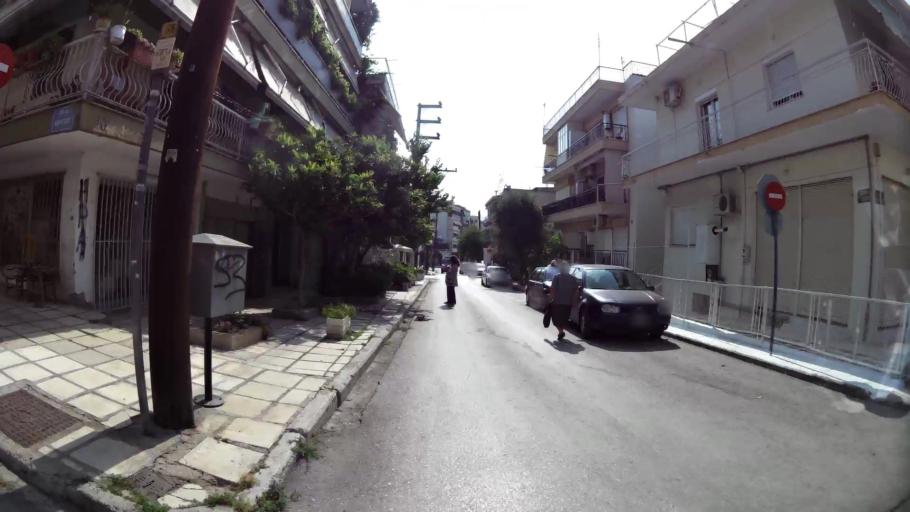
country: GR
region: Central Macedonia
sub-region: Nomos Thessalonikis
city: Stavroupoli
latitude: 40.6680
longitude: 22.9298
